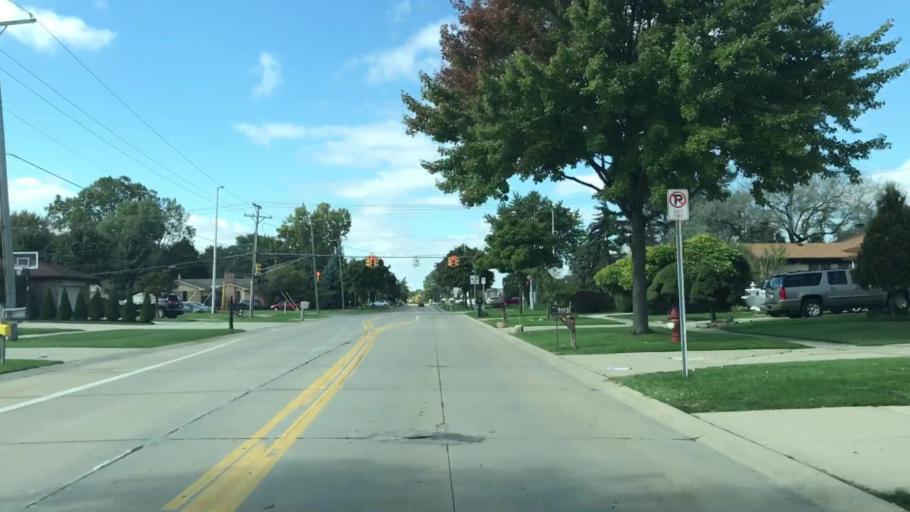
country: US
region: Michigan
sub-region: Macomb County
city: Sterling Heights
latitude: 42.5720
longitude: -83.0690
